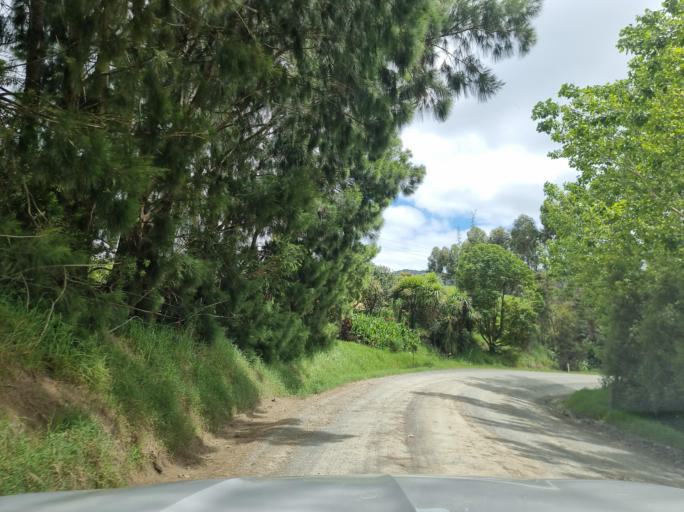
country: NZ
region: Auckland
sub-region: Auckland
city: Wellsford
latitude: -36.0845
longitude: 174.5528
